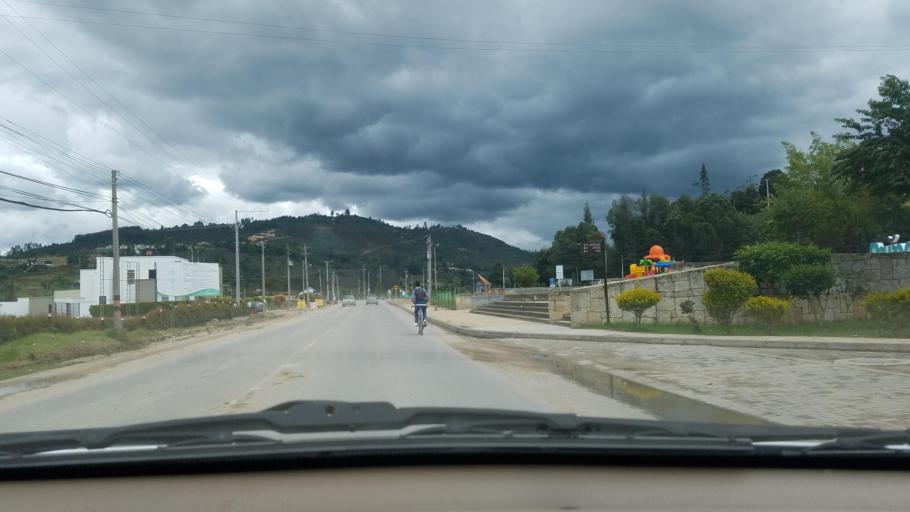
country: CO
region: Boyaca
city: Paipa
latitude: 5.7656
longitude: -73.1114
